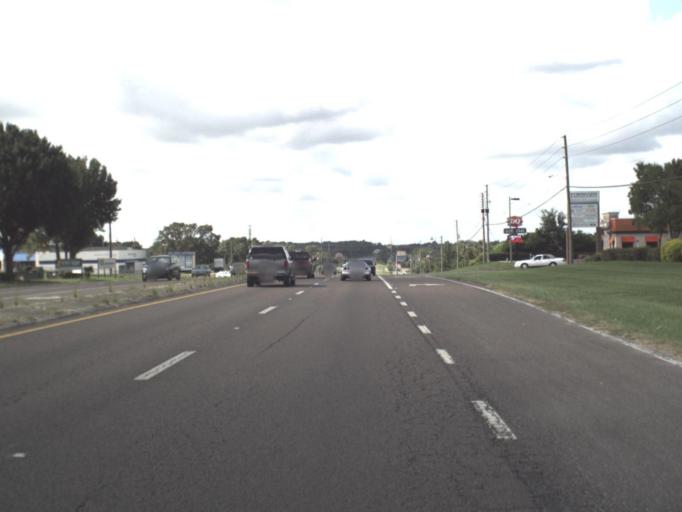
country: US
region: Florida
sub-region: Pasco County
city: Zephyrhills North
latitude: 28.2642
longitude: -82.1882
